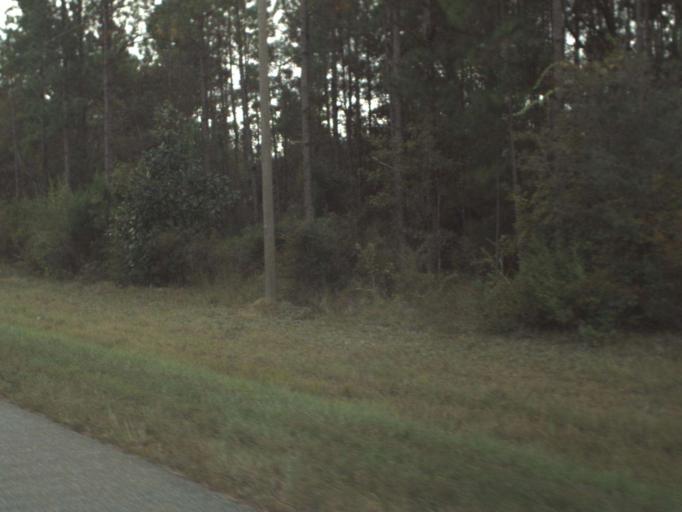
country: US
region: Florida
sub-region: Calhoun County
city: Blountstown
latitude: 30.3731
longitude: -85.2151
